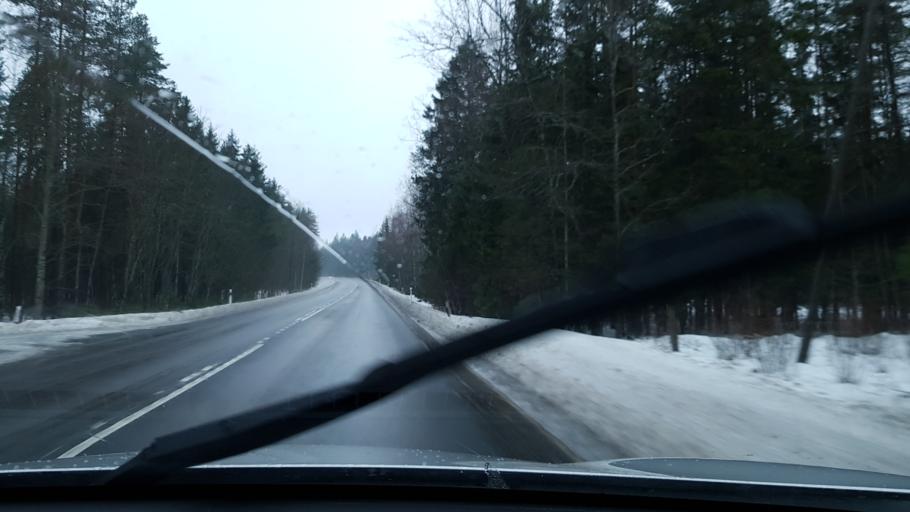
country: EE
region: Raplamaa
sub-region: Maerjamaa vald
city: Marjamaa
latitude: 58.9337
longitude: 24.3650
